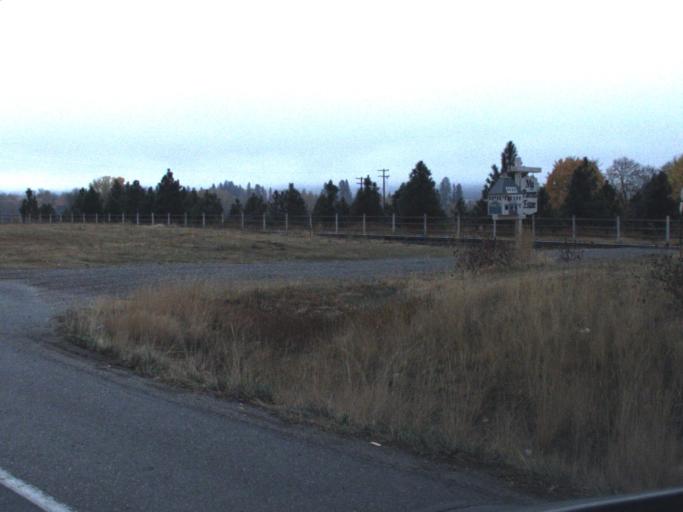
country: US
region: Washington
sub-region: Stevens County
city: Kettle Falls
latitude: 48.6050
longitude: -118.0257
